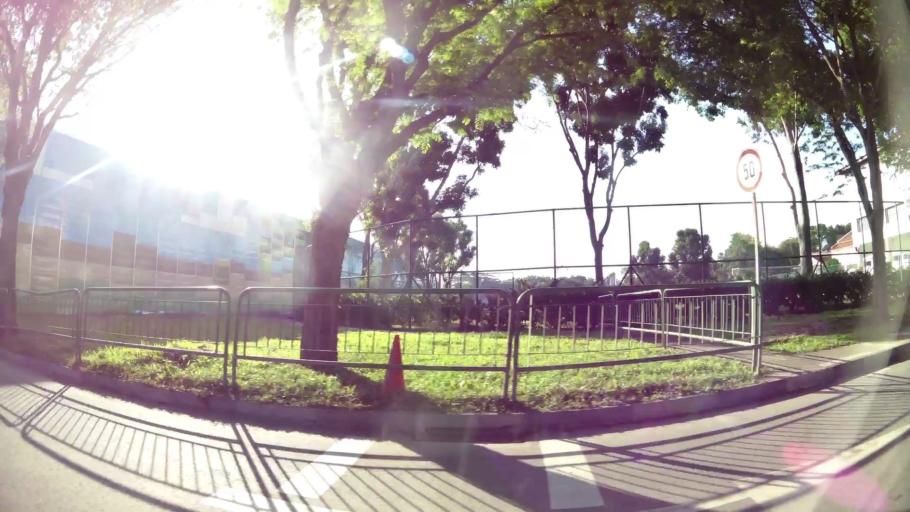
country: SG
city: Singapore
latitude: 1.3172
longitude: 103.9482
